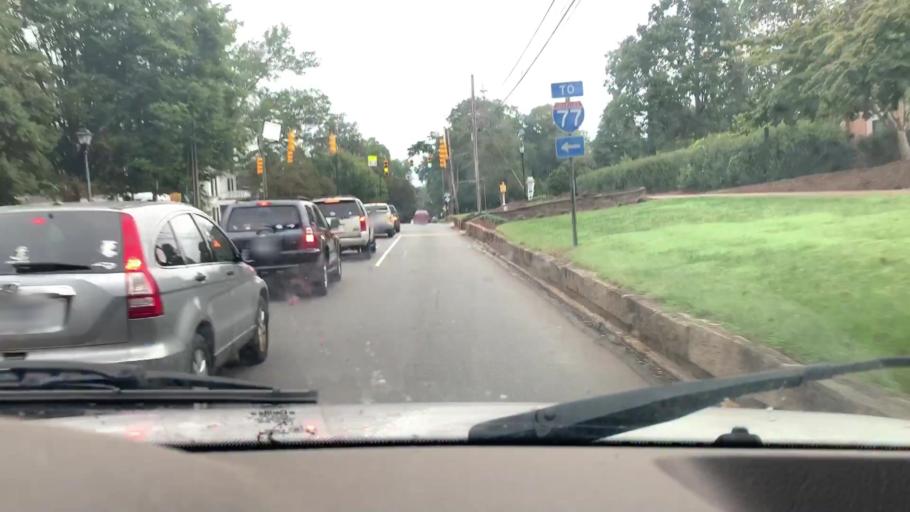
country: US
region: North Carolina
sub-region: Gaston County
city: Davidson
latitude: 35.5014
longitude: -80.8475
